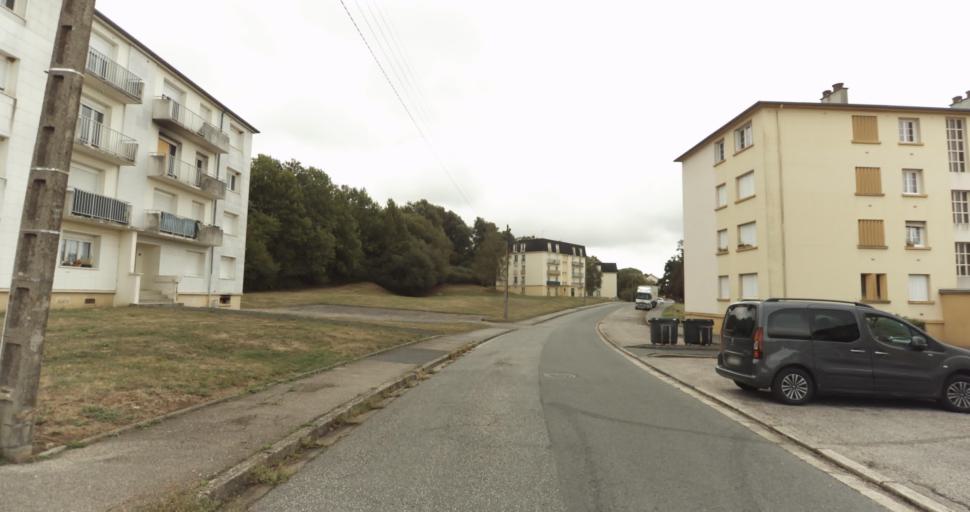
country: FR
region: Lower Normandy
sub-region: Departement de l'Orne
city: Vimoutiers
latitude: 48.9334
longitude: 0.2039
